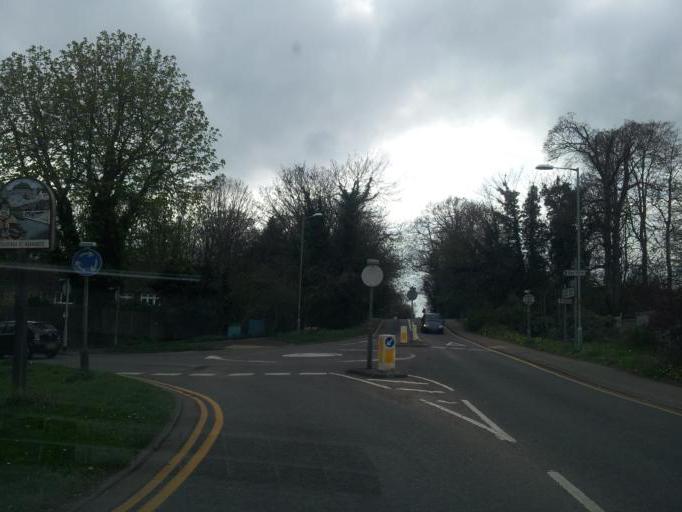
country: GB
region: England
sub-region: Hertfordshire
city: Hoddesdon
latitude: 51.7875
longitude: -0.0001
